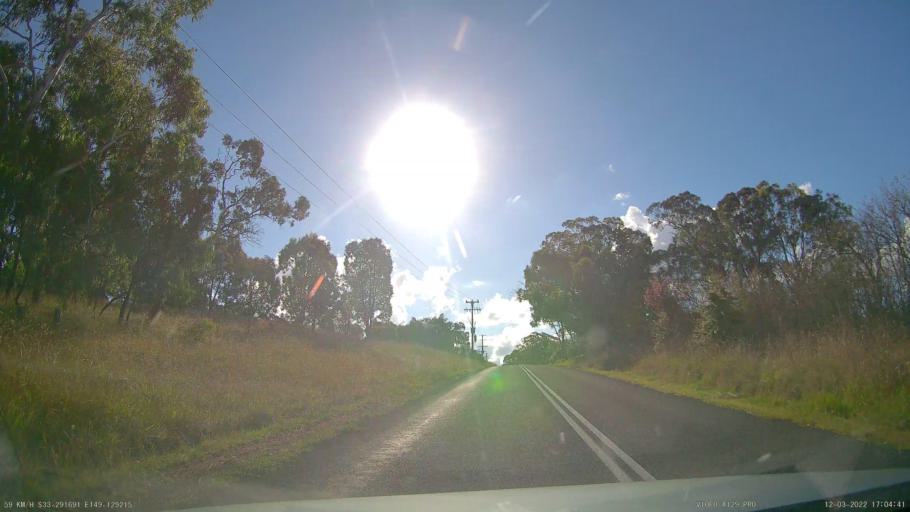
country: AU
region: New South Wales
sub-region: Orange Municipality
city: Orange
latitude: -33.2916
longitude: 149.1290
